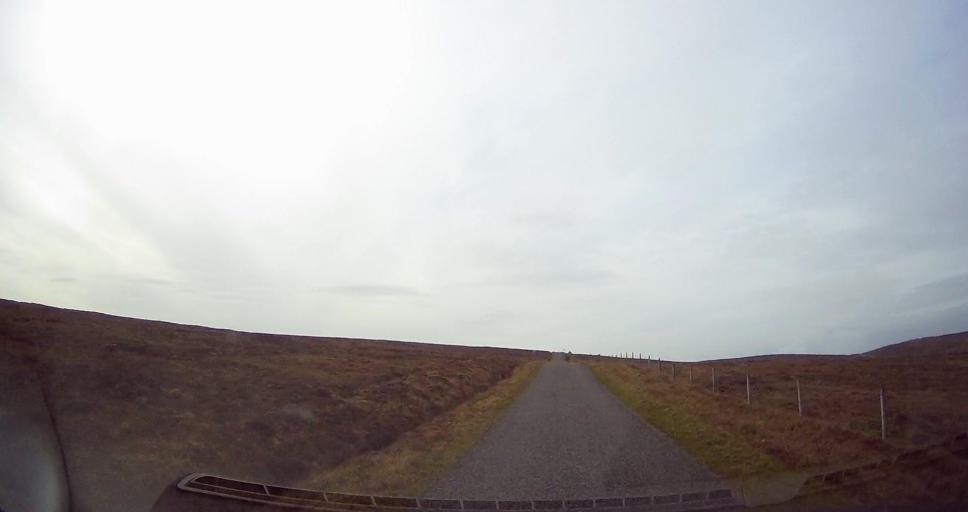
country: GB
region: Scotland
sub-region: Shetland Islands
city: Shetland
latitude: 60.1511
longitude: -1.0852
